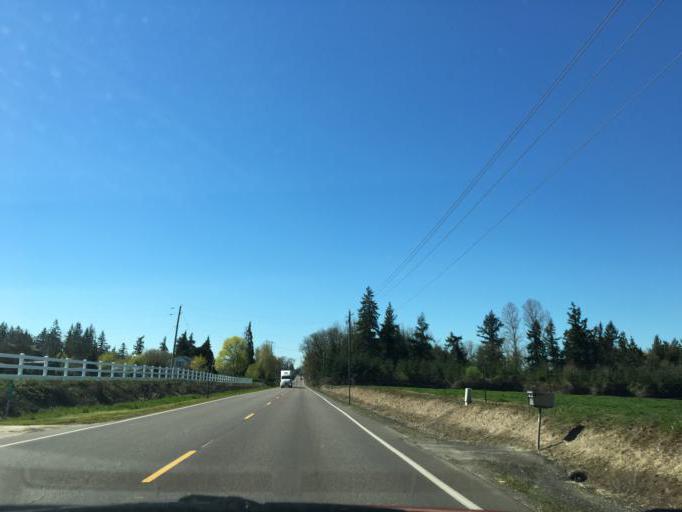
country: US
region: Oregon
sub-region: Marion County
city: Hubbard
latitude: 45.1442
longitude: -122.7409
